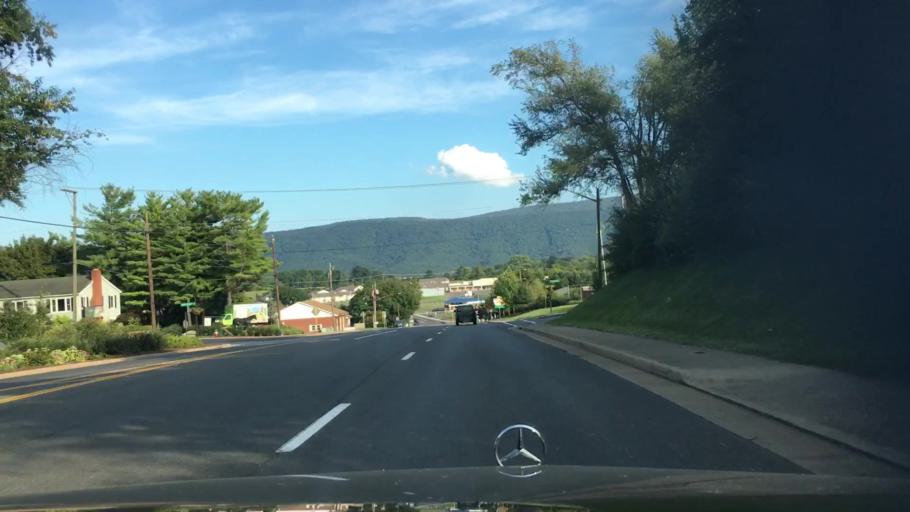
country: US
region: Virginia
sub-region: Shenandoah County
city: Woodstock
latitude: 38.8691
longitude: -78.5219
